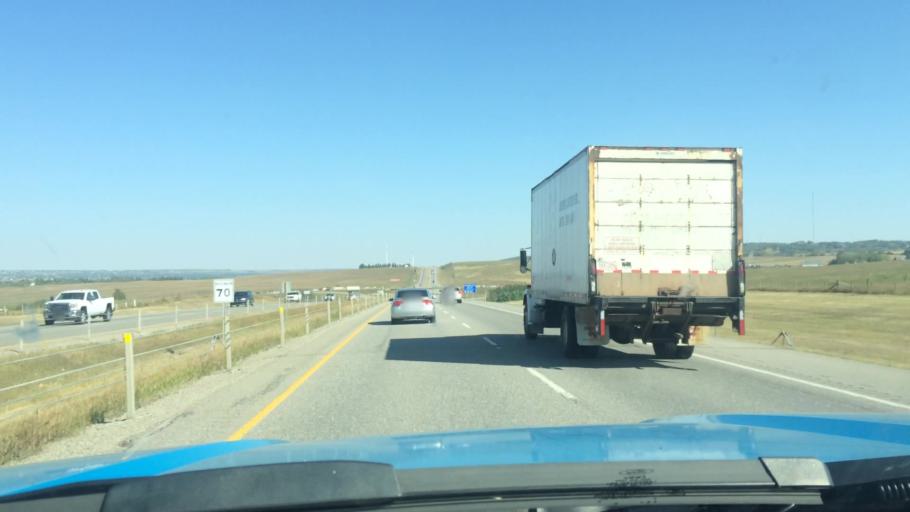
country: CA
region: Alberta
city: Cochrane
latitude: 51.0884
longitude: -114.3166
